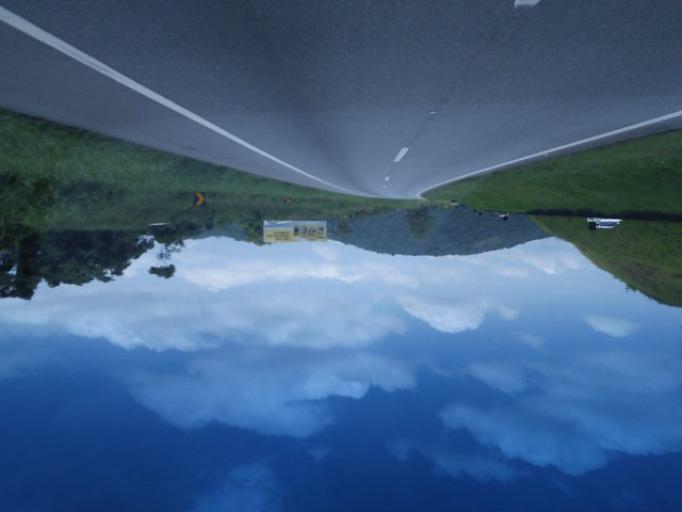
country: BR
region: Sao Paulo
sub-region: Miracatu
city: Miracatu
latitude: -24.2005
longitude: -47.3706
